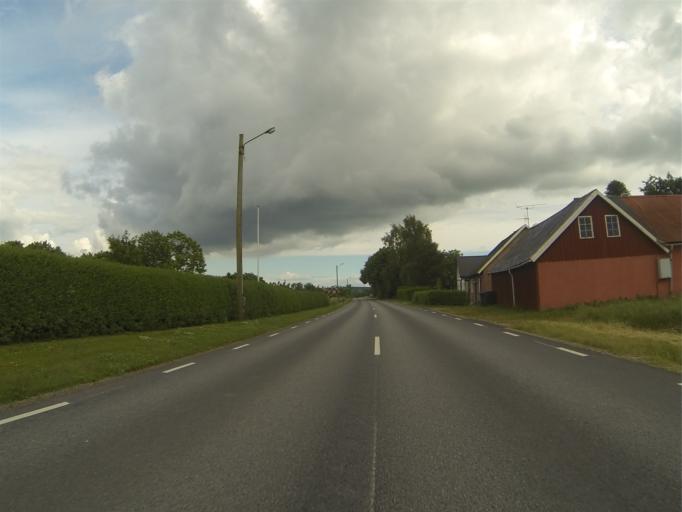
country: SE
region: Skane
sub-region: Eslovs Kommun
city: Eslov
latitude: 55.7348
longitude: 13.3327
